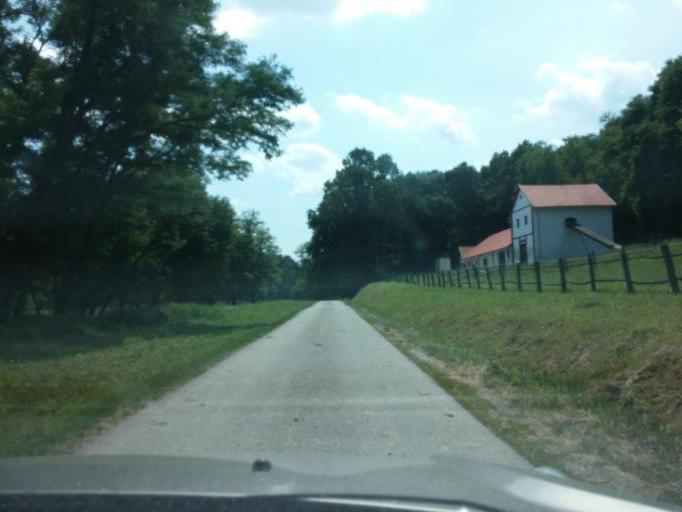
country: HU
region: Somogy
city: Kaposvar
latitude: 46.2529
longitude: 17.7796
